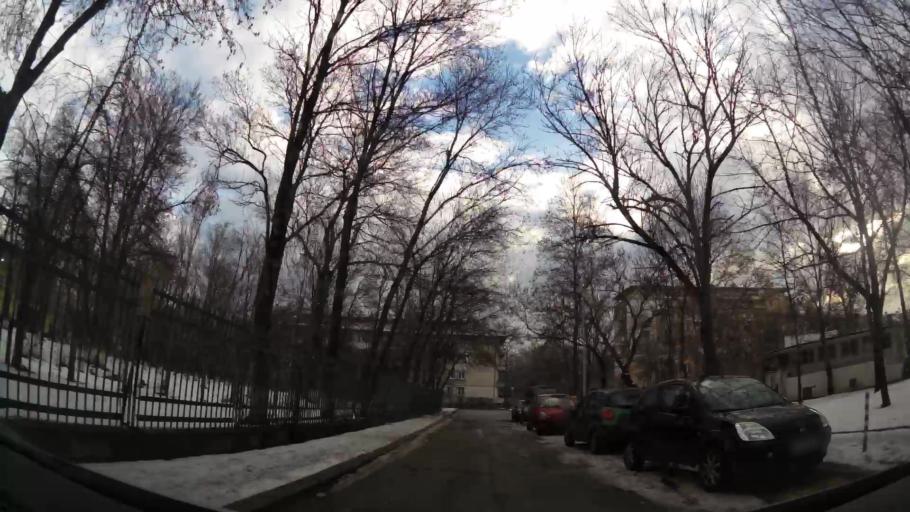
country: BG
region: Sofia-Capital
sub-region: Stolichna Obshtina
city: Sofia
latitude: 42.7043
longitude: 23.2824
